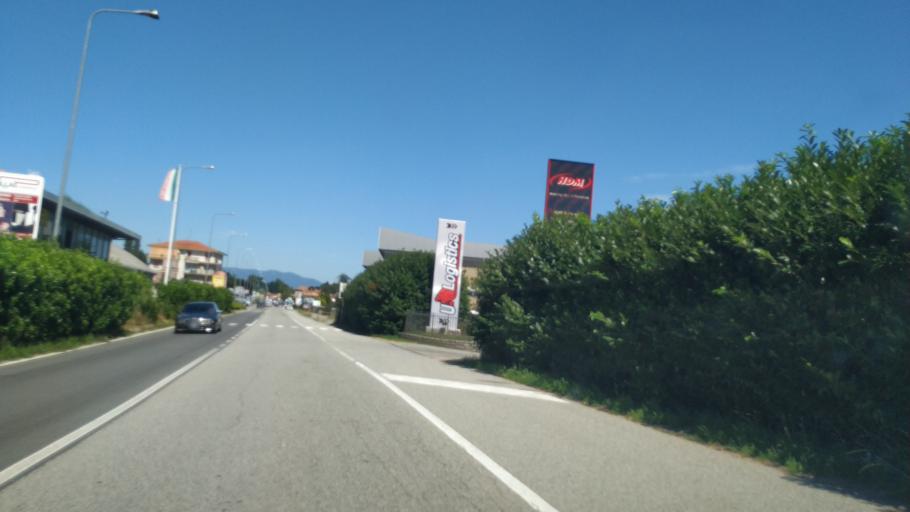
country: IT
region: Piedmont
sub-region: Provincia di Novara
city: Paruzzaro
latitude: 45.7434
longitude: 8.5178
